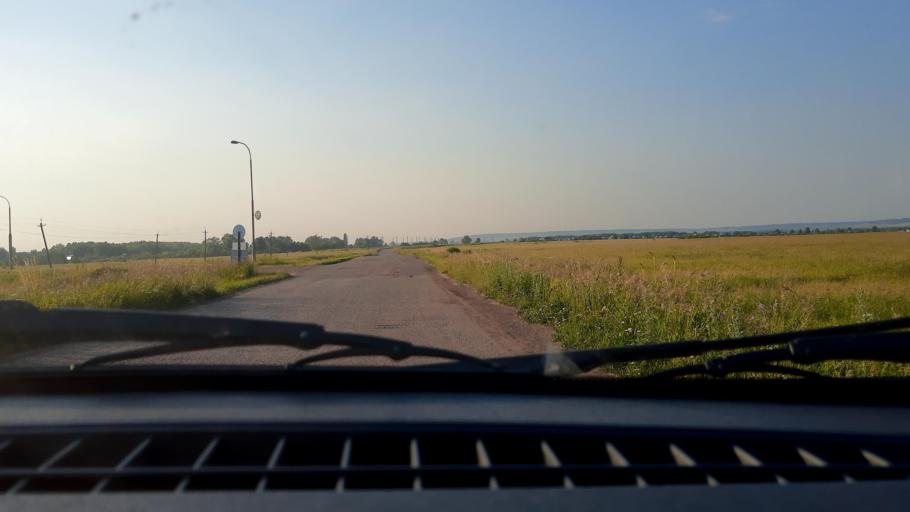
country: RU
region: Bashkortostan
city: Asanovo
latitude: 54.9048
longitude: 55.6281
